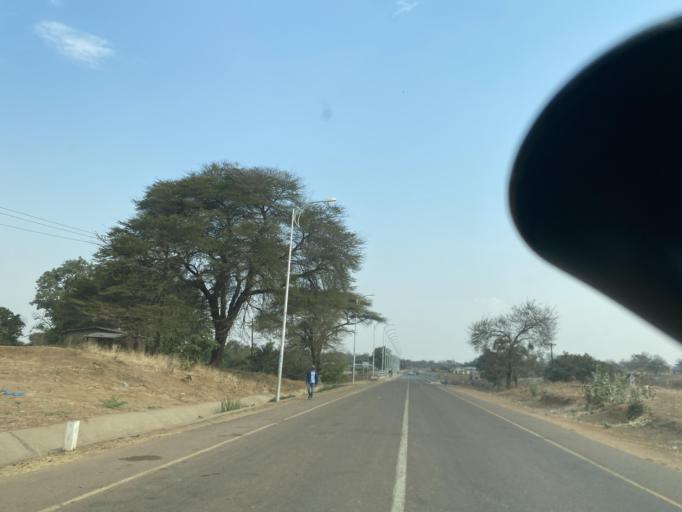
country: ZW
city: Chirundu
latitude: -15.9437
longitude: 28.8747
